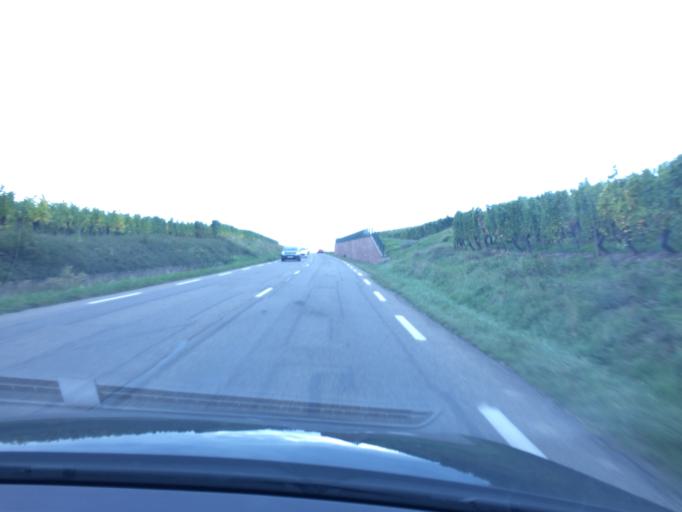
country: FR
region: Alsace
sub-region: Departement du Haut-Rhin
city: Ribeauville
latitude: 48.1766
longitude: 7.3236
